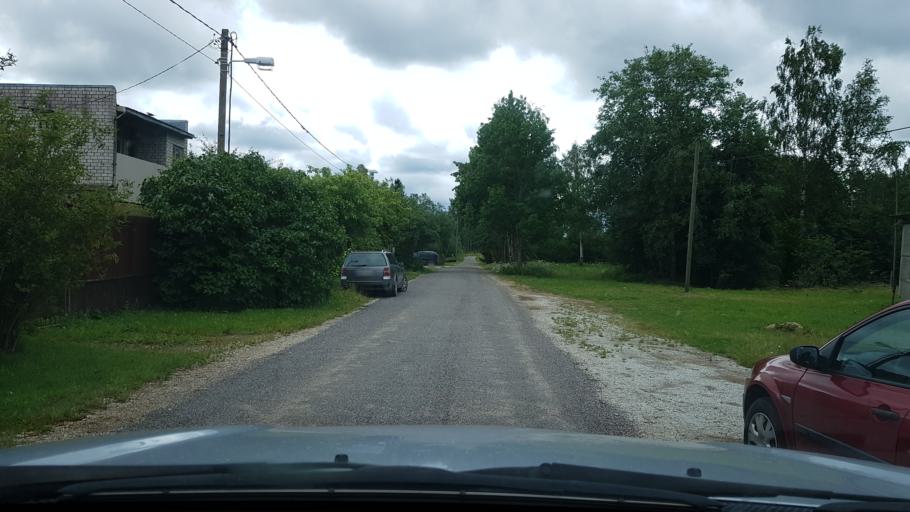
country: EE
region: Ida-Virumaa
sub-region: Sillamaee linn
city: Sillamae
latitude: 59.3686
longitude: 27.7621
